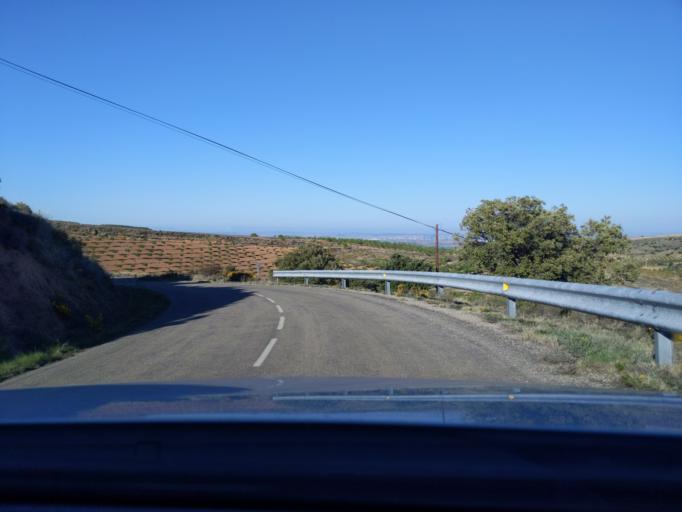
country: ES
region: La Rioja
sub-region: Provincia de La Rioja
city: Bergasillas Bajera
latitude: 42.2457
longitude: -2.1459
